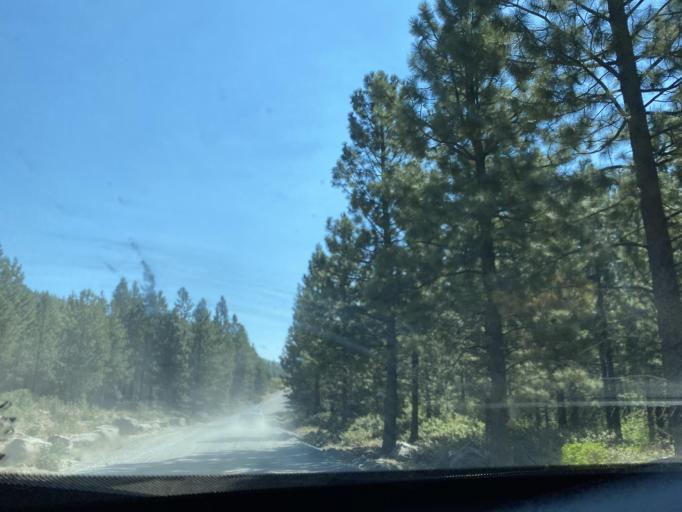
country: US
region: Oregon
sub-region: Deschutes County
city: Sunriver
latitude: 44.0346
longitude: -121.5403
